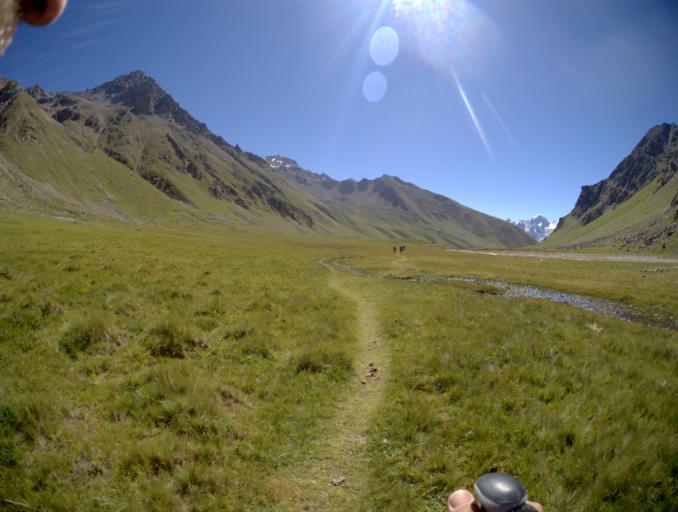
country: RU
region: Kabardino-Balkariya
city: Terskol
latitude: 43.3205
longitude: 42.5752
